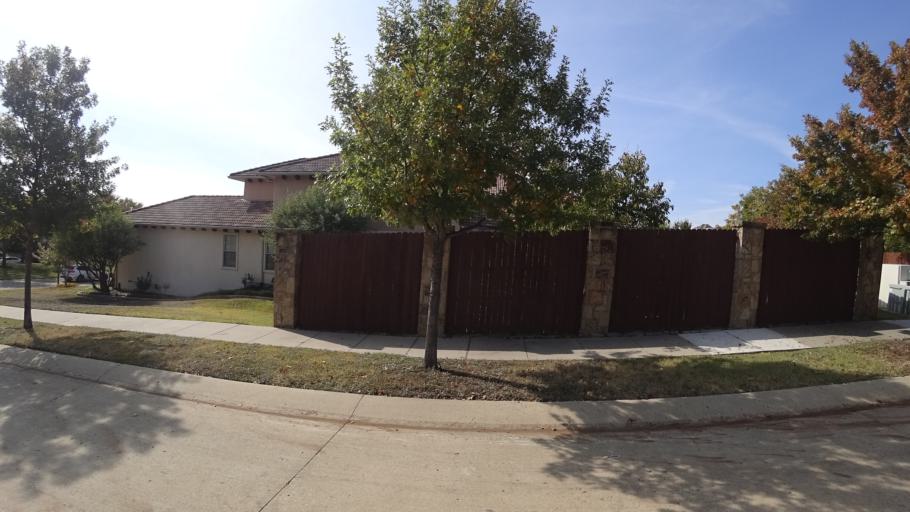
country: US
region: Texas
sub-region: Denton County
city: The Colony
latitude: 33.0373
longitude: -96.8951
